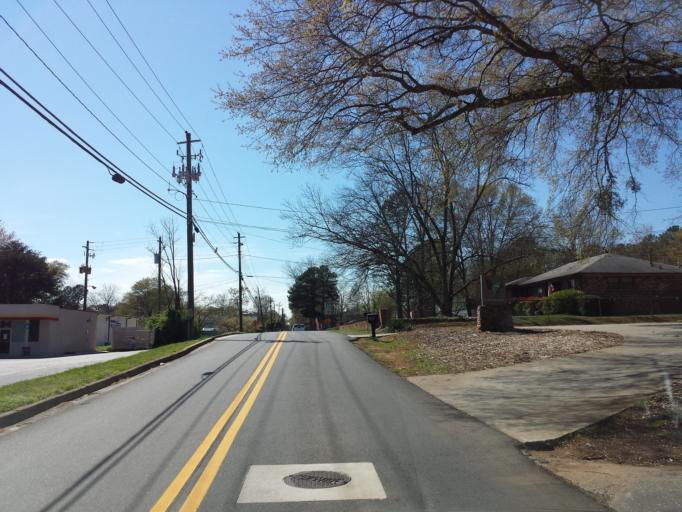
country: US
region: Georgia
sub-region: Cobb County
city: Smyrna
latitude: 33.8836
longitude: -84.5026
